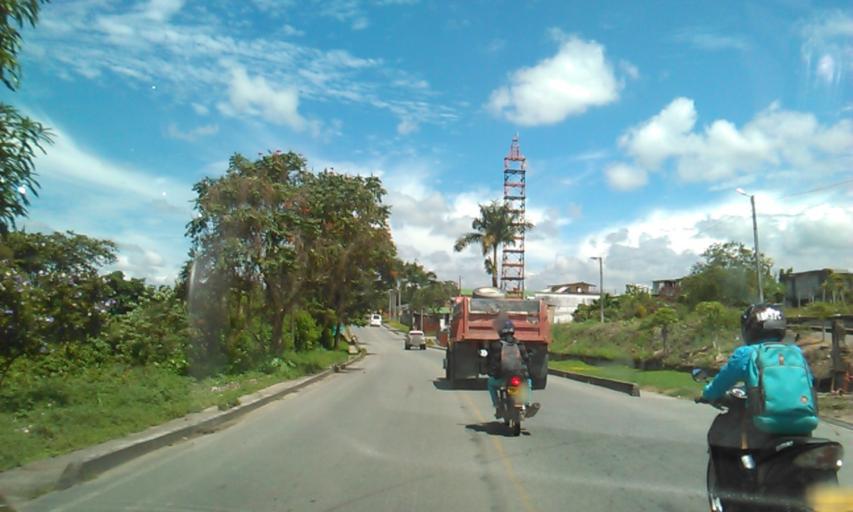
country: CO
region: Quindio
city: Cordoba
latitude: 4.4296
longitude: -75.7183
